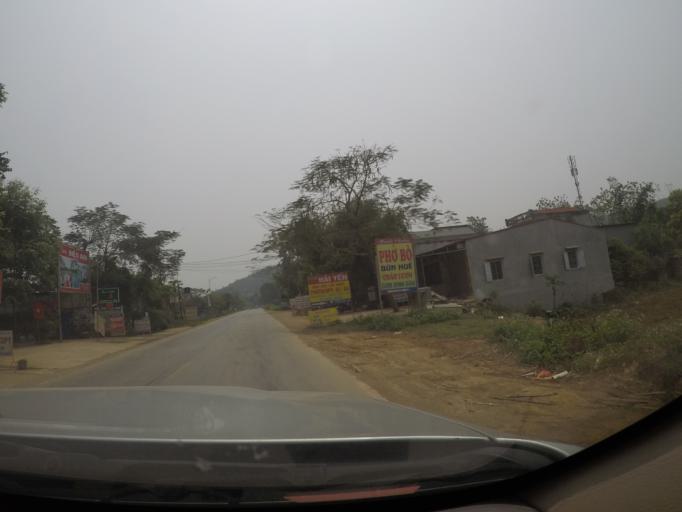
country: VN
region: Thanh Hoa
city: Thi Tran Thuong Xuan
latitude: 19.9631
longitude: 105.3981
